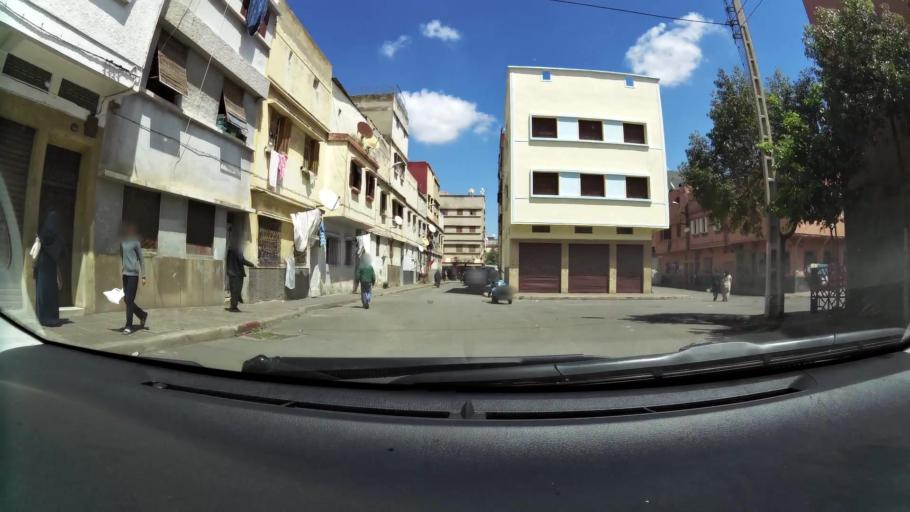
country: MA
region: Grand Casablanca
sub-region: Casablanca
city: Casablanca
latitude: 33.5589
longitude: -7.5834
